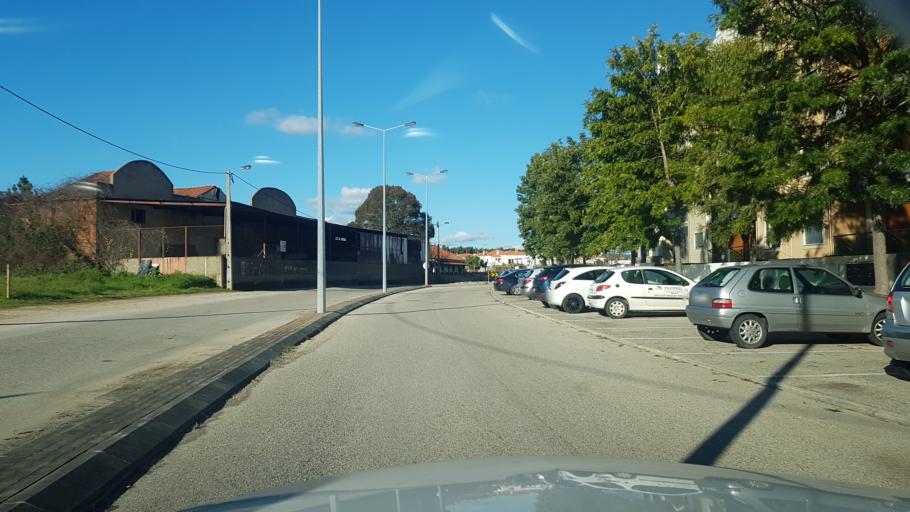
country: PT
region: Santarem
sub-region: Entroncamento
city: Entroncamento
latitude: 39.4767
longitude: -8.4737
